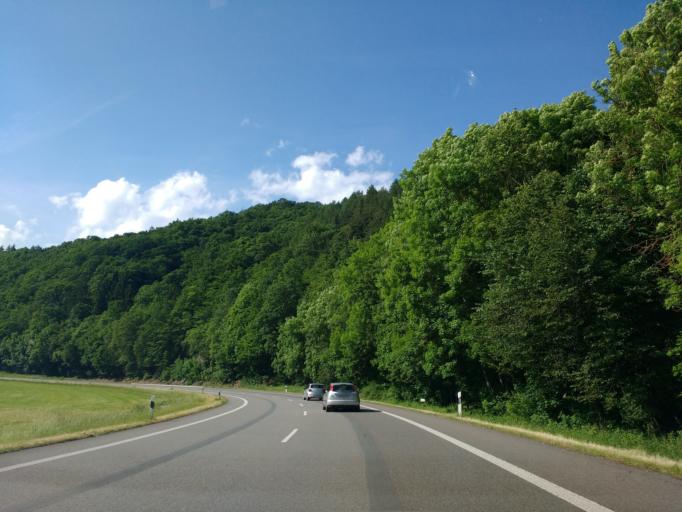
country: DE
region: Hesse
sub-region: Regierungsbezirk Kassel
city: Vohl
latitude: 51.1891
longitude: 8.8955
